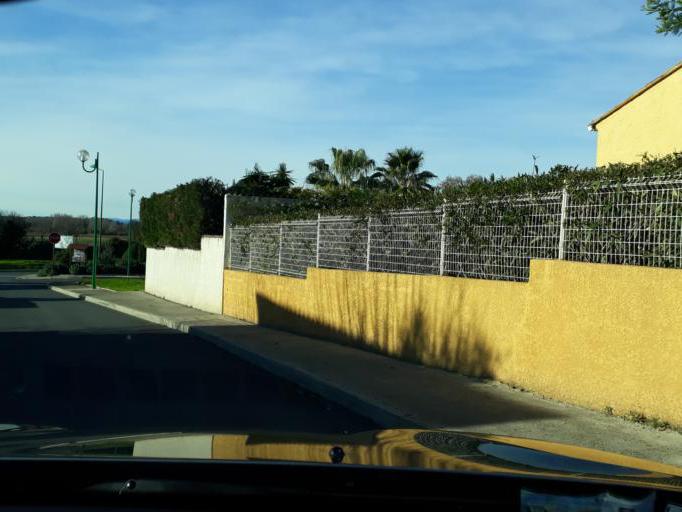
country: FR
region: Languedoc-Roussillon
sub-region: Departement de l'Herault
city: Castelnau-de-Guers
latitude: 43.4421
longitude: 3.4420
